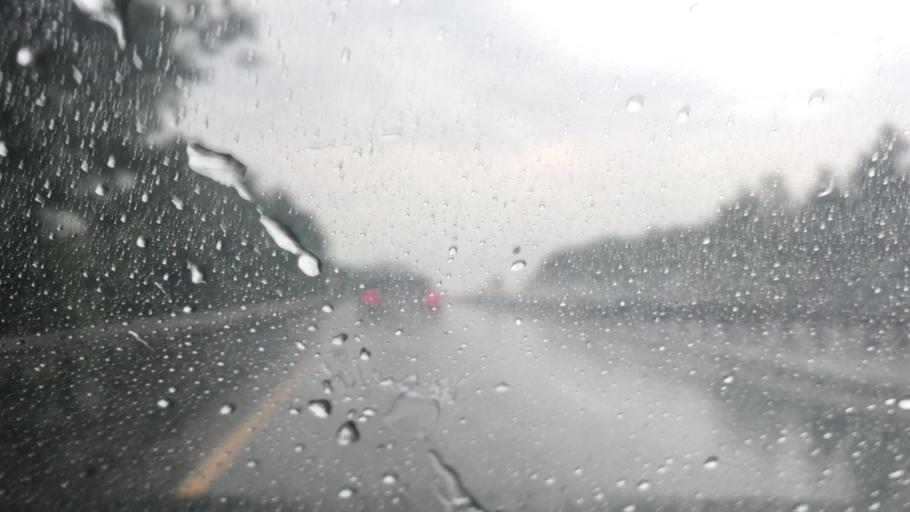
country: US
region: New Jersey
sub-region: Monmouth County
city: Tinton Falls
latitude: 40.2743
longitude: -74.0808
